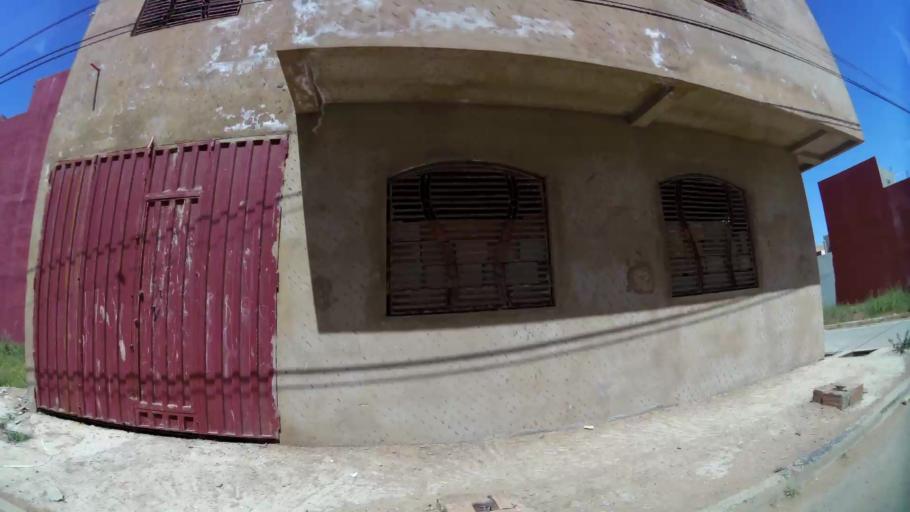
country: MA
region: Rabat-Sale-Zemmour-Zaer
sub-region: Khemisset
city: Khemisset
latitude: 33.8115
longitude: -6.0900
